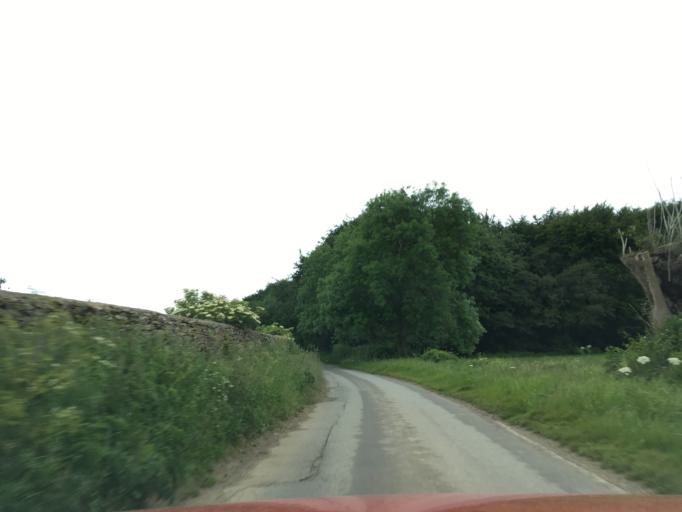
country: GB
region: England
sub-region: Wiltshire
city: Luckington
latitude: 51.5723
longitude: -2.2683
